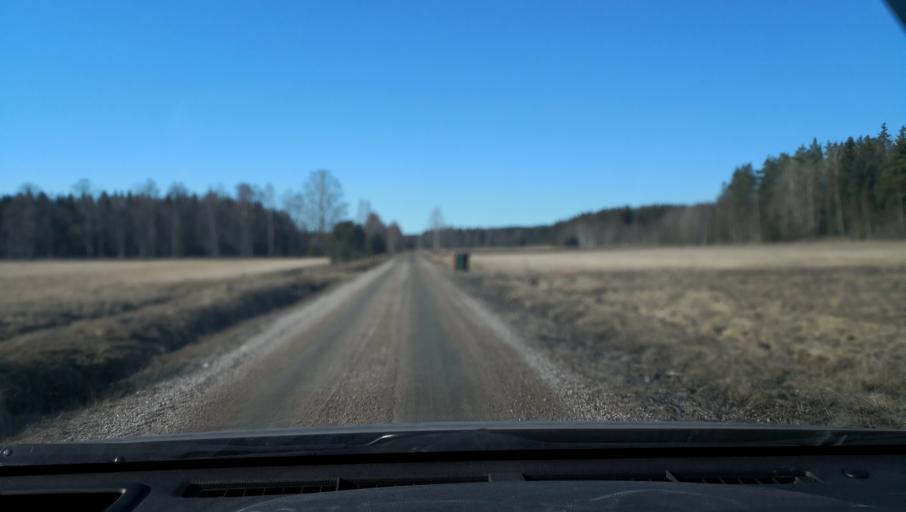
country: SE
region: Vaestmanland
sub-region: Sala Kommun
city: Sala
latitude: 60.1268
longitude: 16.6550
